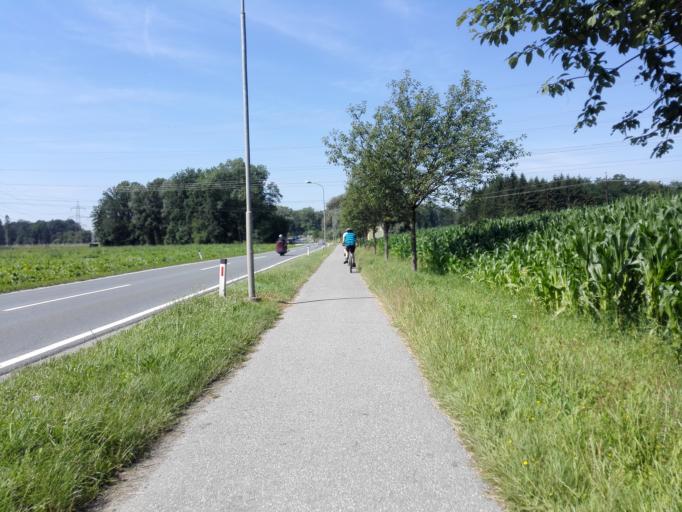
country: AT
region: Styria
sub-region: Politischer Bezirk Graz-Umgebung
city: Fernitz
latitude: 46.9701
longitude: 15.4927
